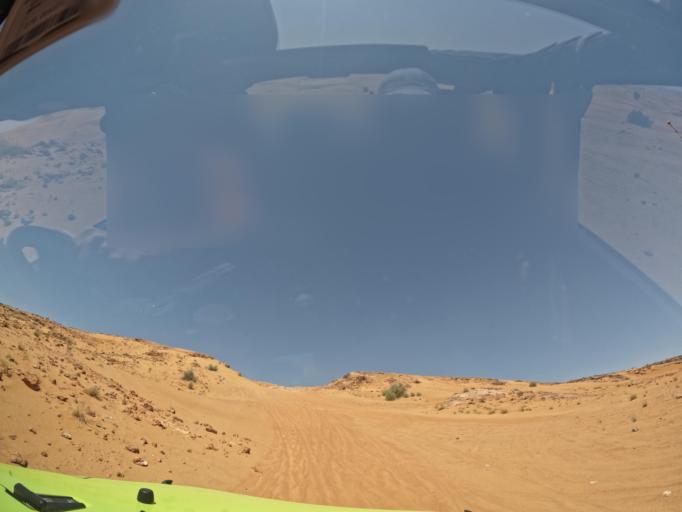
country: AE
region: Ash Shariqah
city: Adh Dhayd
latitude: 25.0190
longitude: 55.7282
